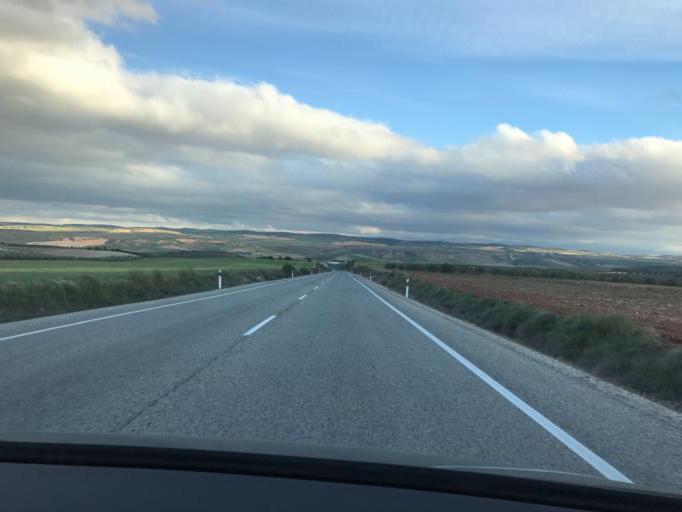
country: ES
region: Andalusia
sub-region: Provincia de Jaen
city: Guadahortuna
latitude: 37.5782
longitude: -3.4041
